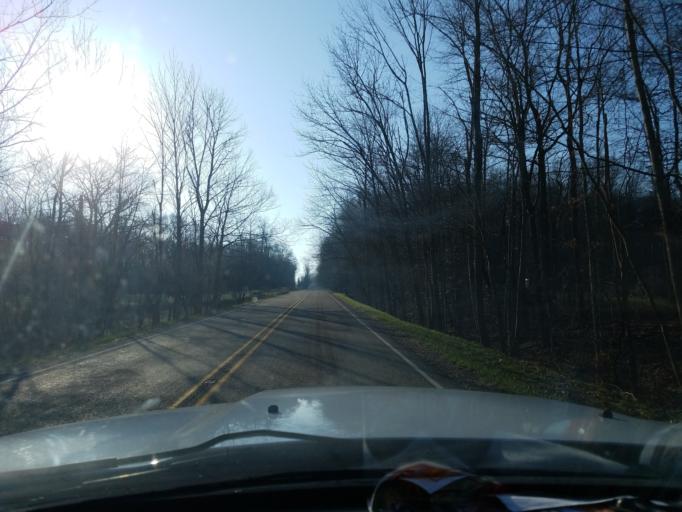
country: US
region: Indiana
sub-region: Owen County
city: Spencer
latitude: 39.3451
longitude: -86.9120
